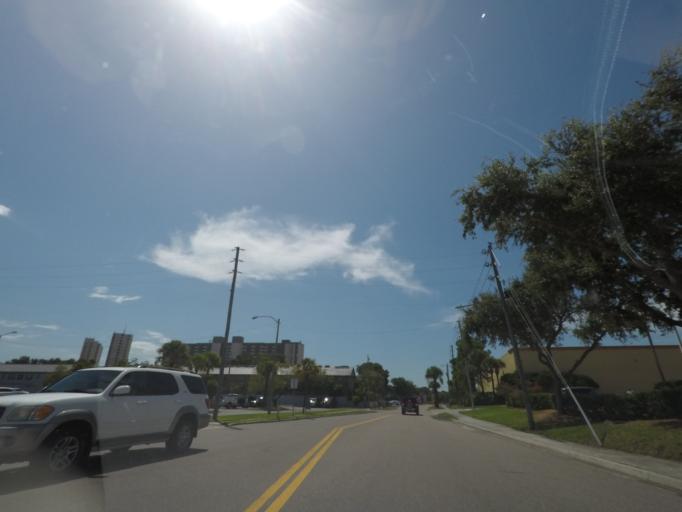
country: US
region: Florida
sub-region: Pinellas County
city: South Pasadena
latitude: 27.7594
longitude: -82.7365
